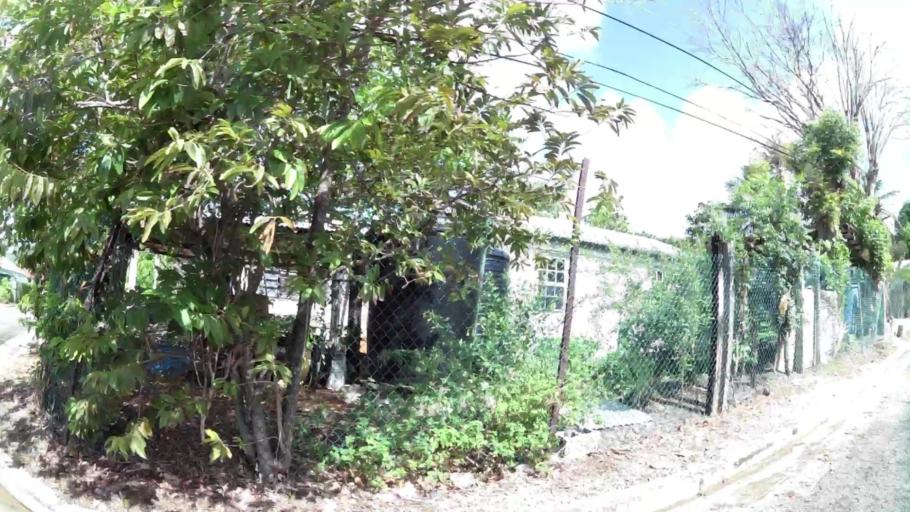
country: AG
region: Saint Mary
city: Bolands
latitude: 17.0645
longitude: -61.8735
